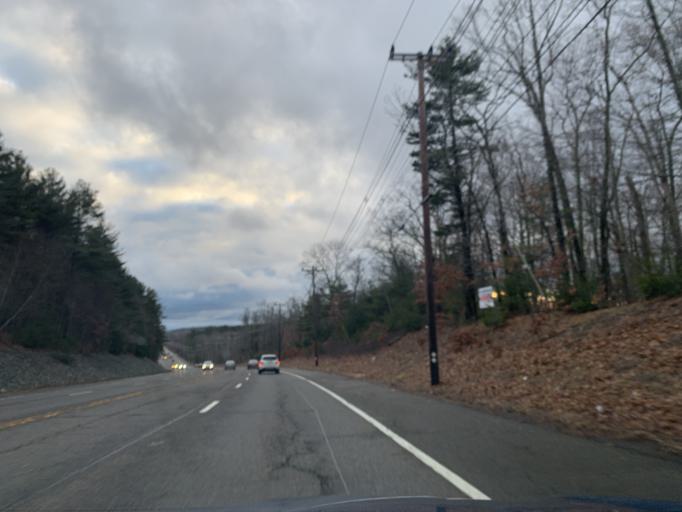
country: US
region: Massachusetts
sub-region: Norfolk County
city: Wrentham
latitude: 42.0703
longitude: -71.2912
